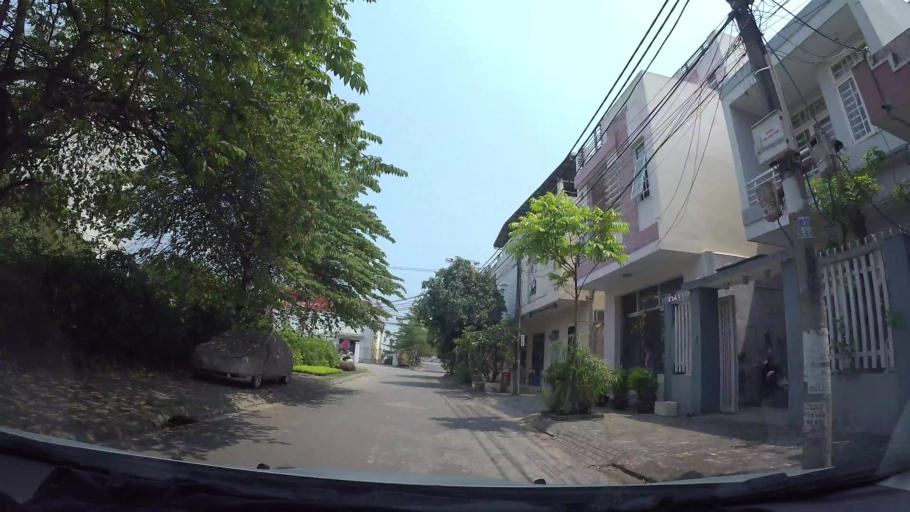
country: VN
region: Da Nang
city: Cam Le
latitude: 16.0189
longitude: 108.2102
